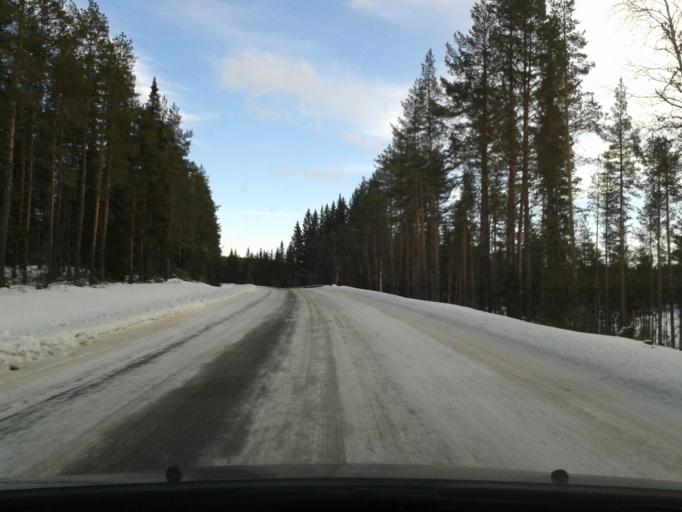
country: SE
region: Vaesterbotten
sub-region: Asele Kommun
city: Asele
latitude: 64.2490
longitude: 17.2780
